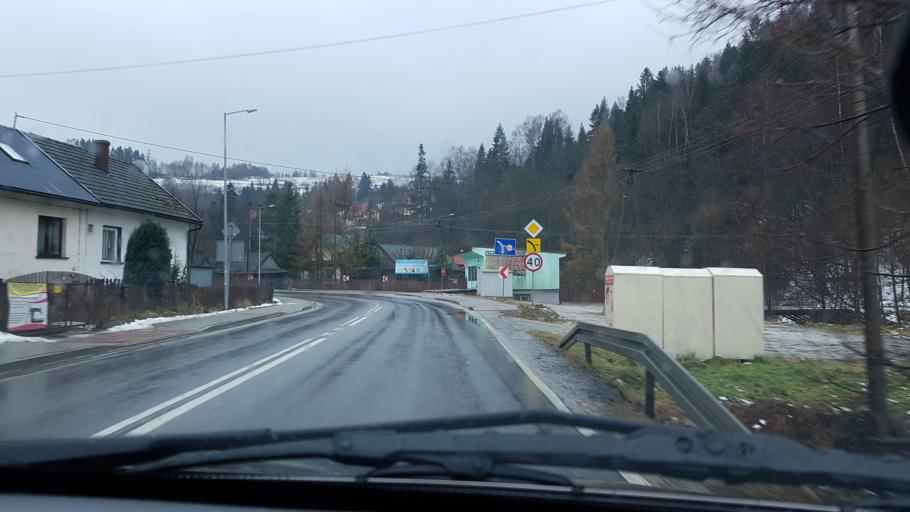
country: PL
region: Lesser Poland Voivodeship
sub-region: Powiat nowotarski
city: Raba Wyzna
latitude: 49.5500
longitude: 19.8840
